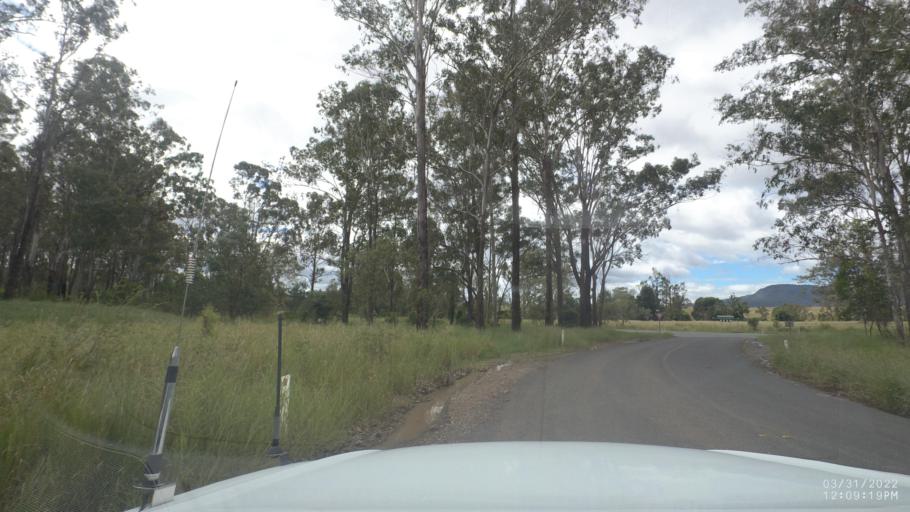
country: AU
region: Queensland
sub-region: Logan
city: Cedar Vale
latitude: -27.9320
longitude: 153.0791
